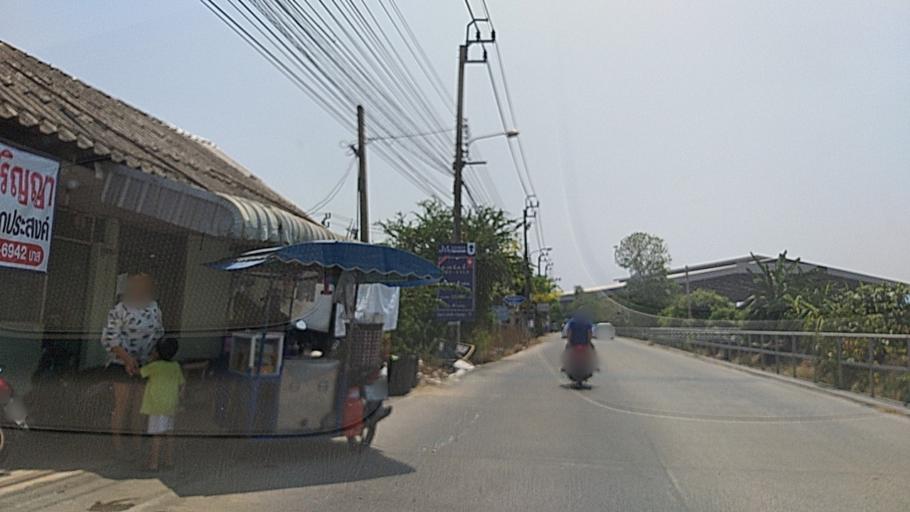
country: TH
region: Nonthaburi
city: Bang Bua Thong
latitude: 13.9116
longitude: 100.3966
